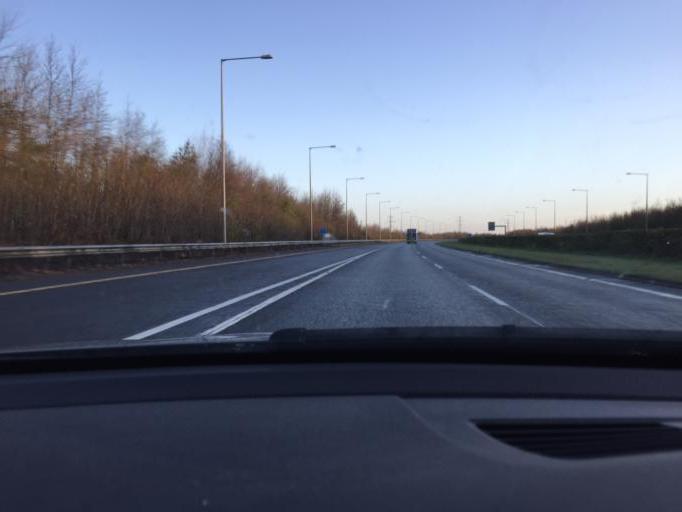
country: IE
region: Leinster
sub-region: Fingal County
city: Swords
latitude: 53.4818
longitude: -6.2068
